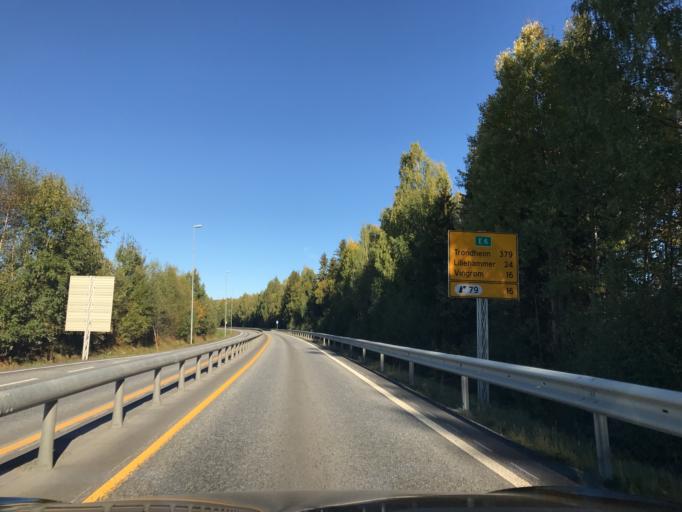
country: NO
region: Hedmark
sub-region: Ringsaker
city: Moelv
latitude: 60.9591
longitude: 10.6228
